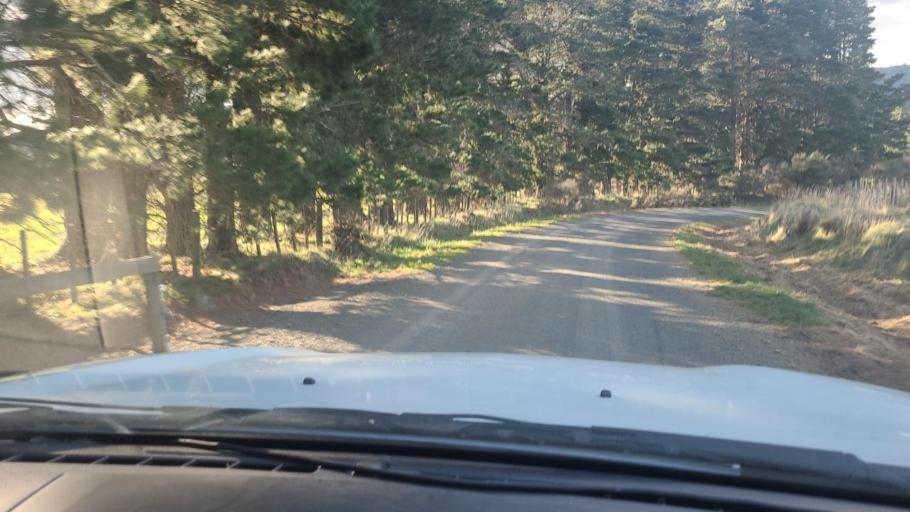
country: NZ
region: Hawke's Bay
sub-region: Hastings District
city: Hastings
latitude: -39.6767
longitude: 176.2890
